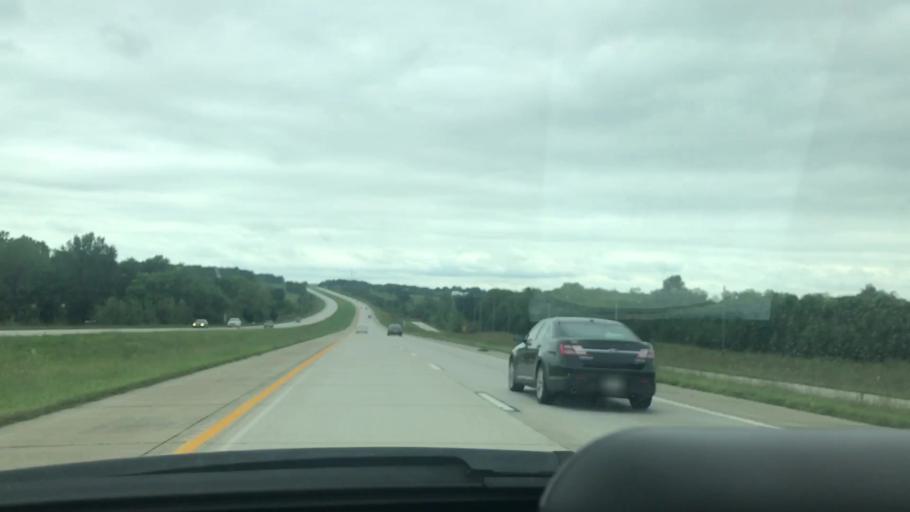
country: US
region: Missouri
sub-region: Dallas County
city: Buffalo
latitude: 37.5247
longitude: -93.1377
